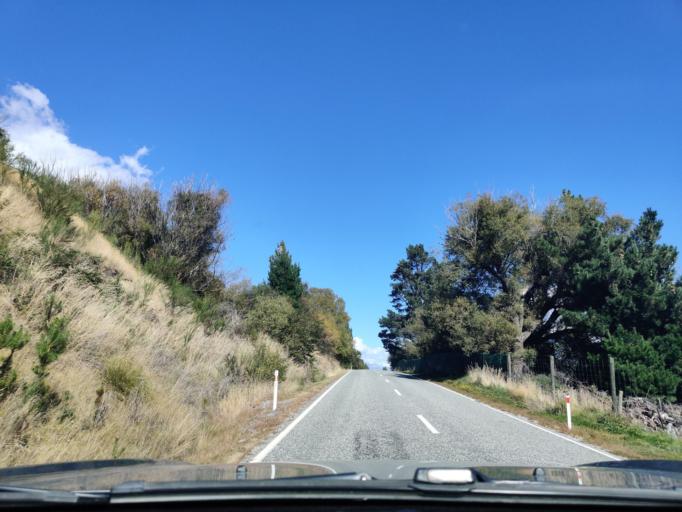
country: NZ
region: Otago
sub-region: Queenstown-Lakes District
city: Queenstown
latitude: -44.8309
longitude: 168.3986
